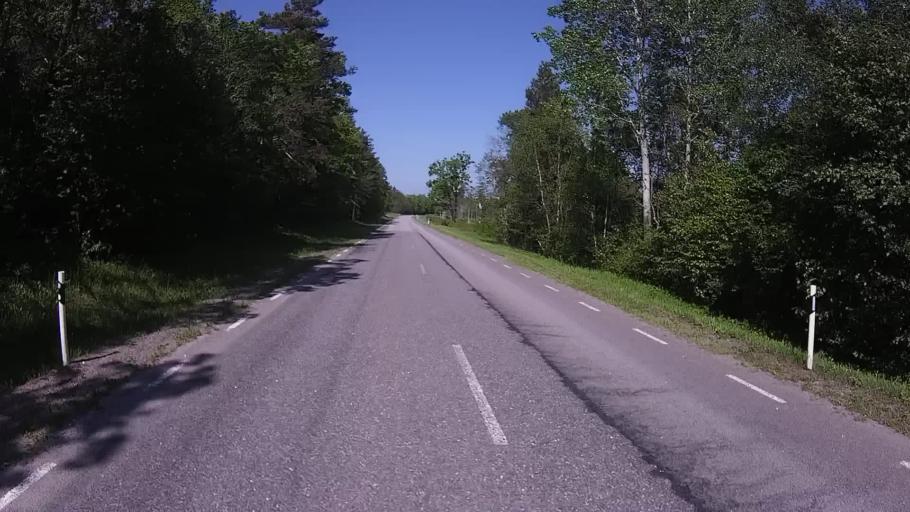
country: EE
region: Saare
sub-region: Kuressaare linn
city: Kuressaare
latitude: 58.4155
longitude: 22.4299
